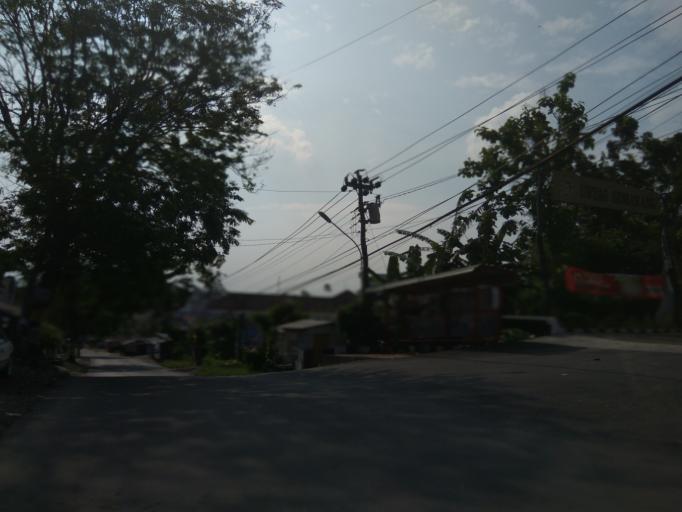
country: ID
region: Central Java
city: Semarang
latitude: -7.0222
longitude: 110.3991
